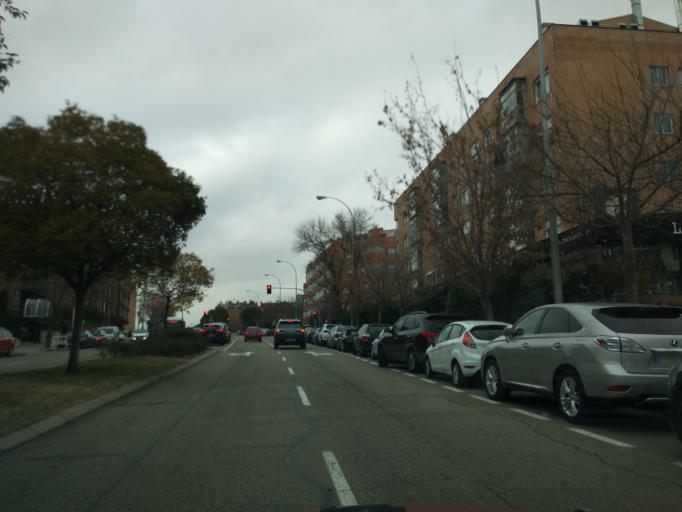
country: ES
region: Madrid
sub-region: Provincia de Madrid
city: San Blas
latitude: 40.4568
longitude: -3.6240
